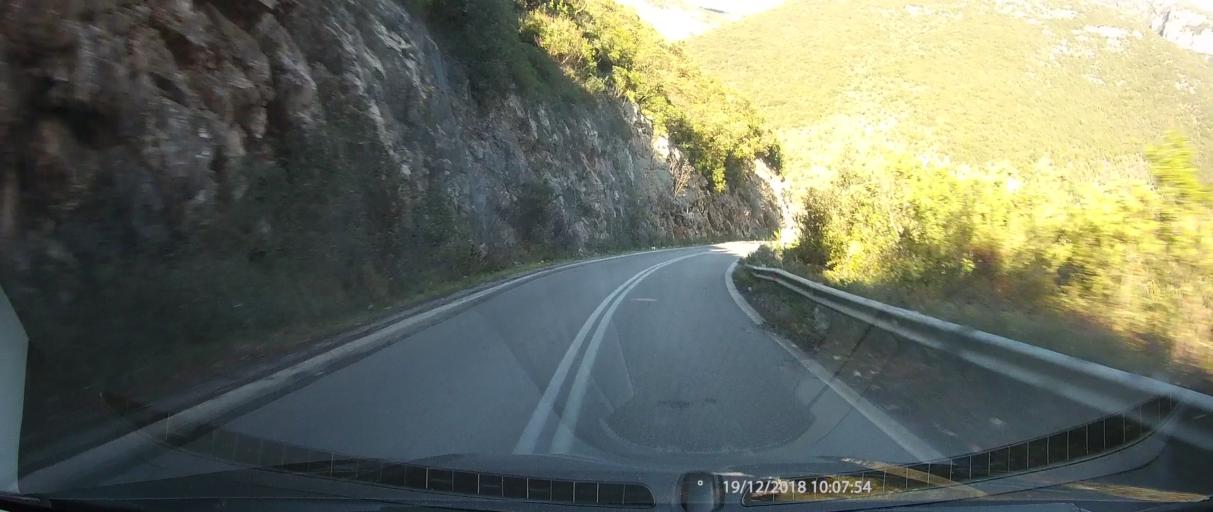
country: GR
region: Peloponnese
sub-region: Nomos Messinias
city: Paralia Vergas
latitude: 37.1152
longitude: 22.2088
